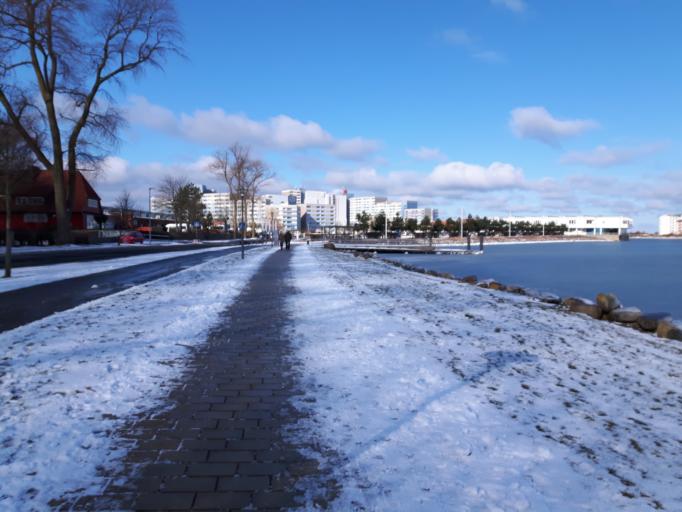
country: DE
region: Schleswig-Holstein
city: Heiligenhafen
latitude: 54.3763
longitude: 10.9572
